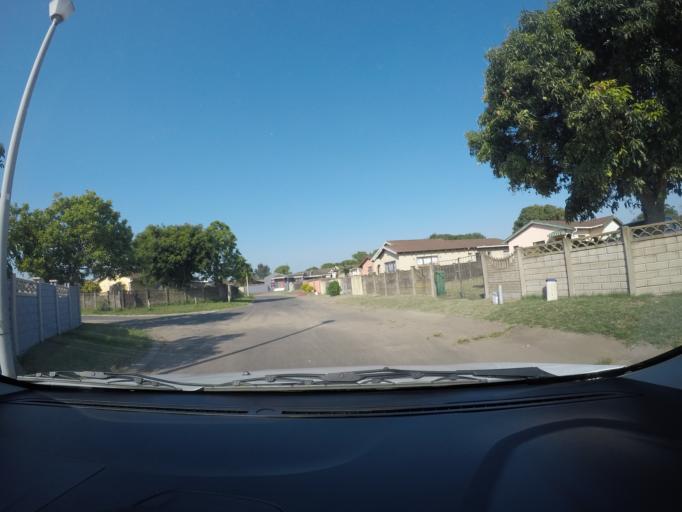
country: ZA
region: KwaZulu-Natal
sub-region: uThungulu District Municipality
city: Richards Bay
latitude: -28.7173
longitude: 32.0365
